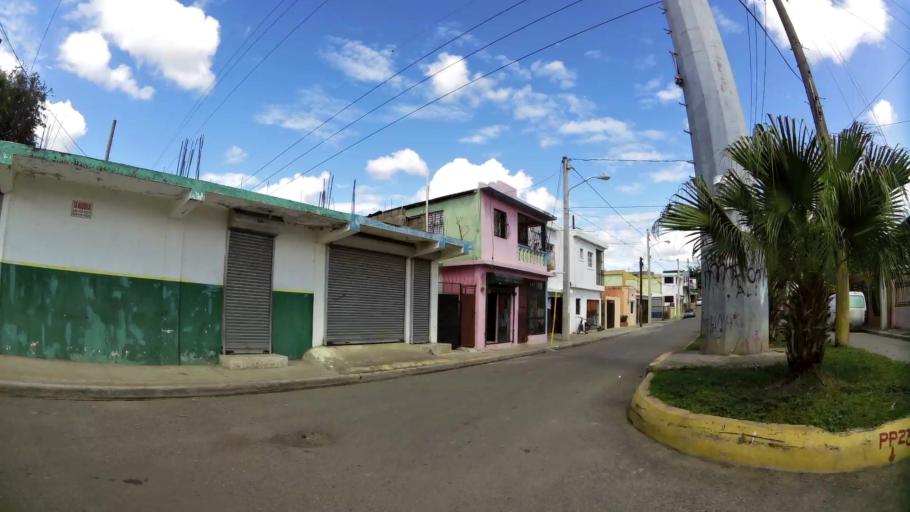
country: DO
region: La Vega
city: Concepcion de La Vega
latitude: 19.2213
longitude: -70.5360
